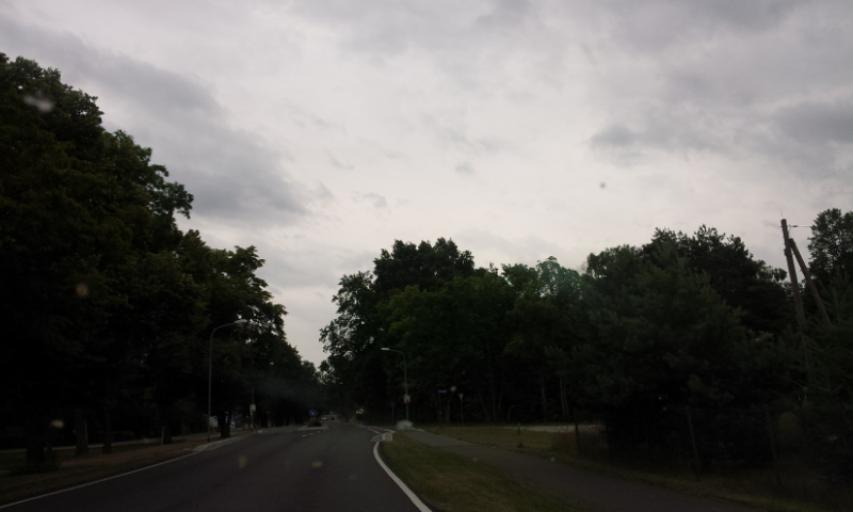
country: DE
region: Brandenburg
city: Niedergorsdorf
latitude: 52.0134
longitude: 13.0013
